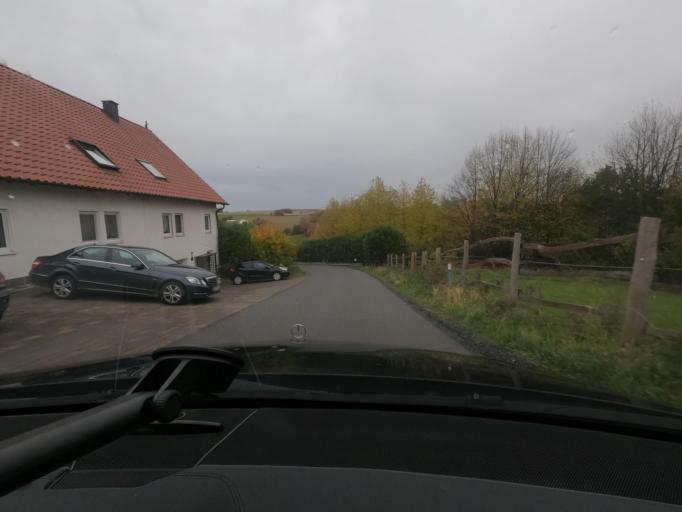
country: DE
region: North Rhine-Westphalia
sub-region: Regierungsbezirk Arnsberg
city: Mohnesee
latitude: 51.4923
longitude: 8.1940
